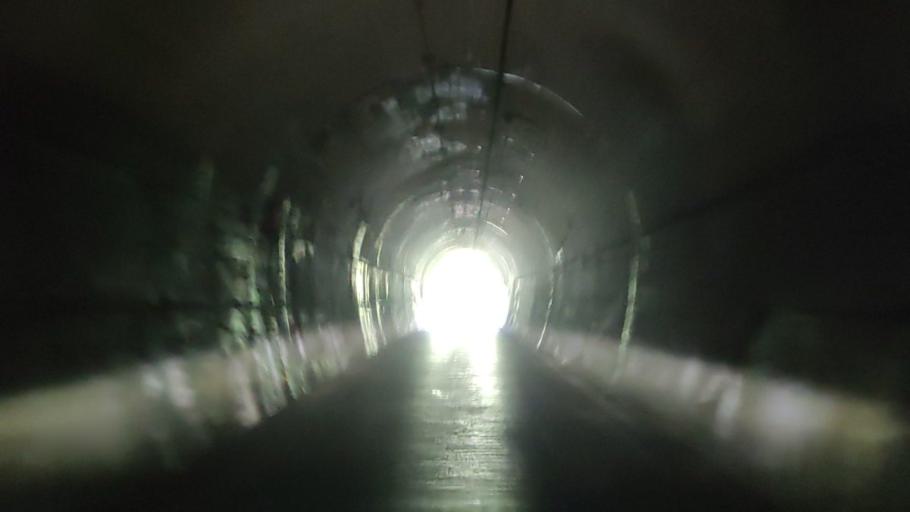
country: JP
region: Wakayama
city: Shingu
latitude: 33.9128
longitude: 135.8777
